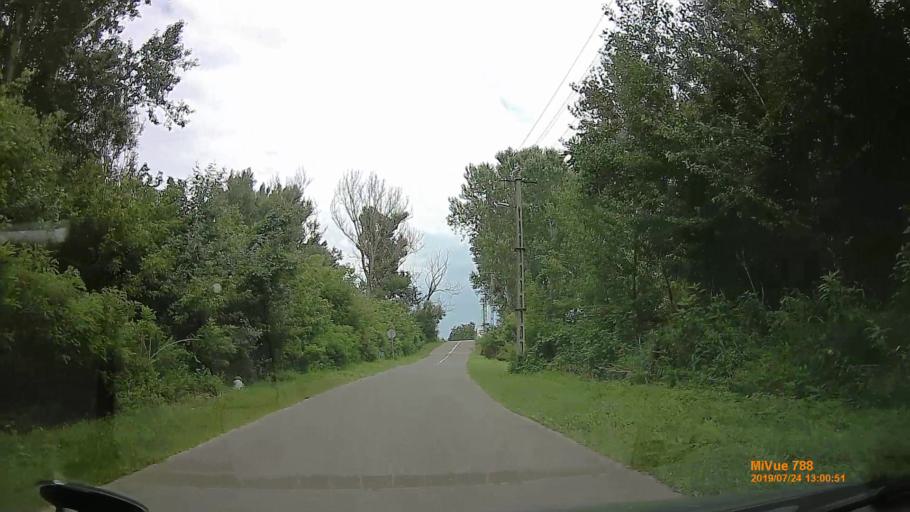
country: HU
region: Szabolcs-Szatmar-Bereg
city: Aranyosapati
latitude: 48.2219
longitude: 22.2827
